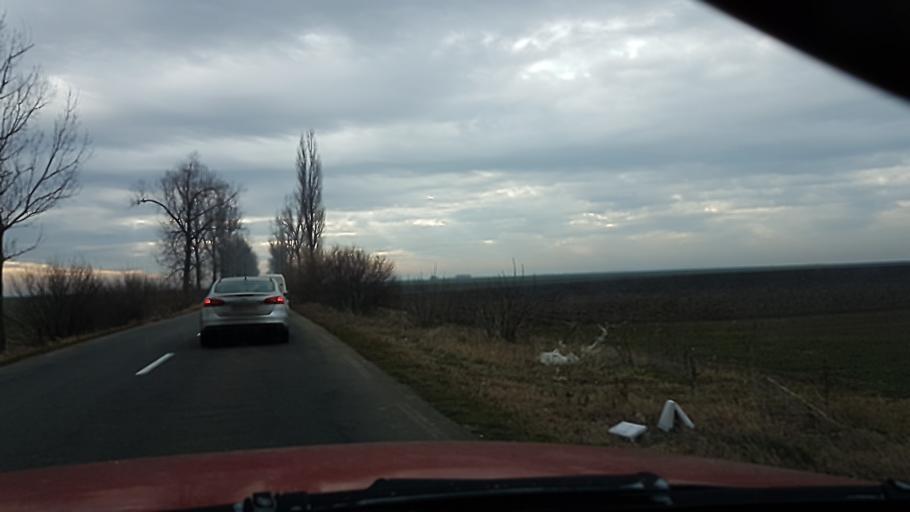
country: RO
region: Giurgiu
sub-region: Comuna Herasti
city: Herasti
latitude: 44.2389
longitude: 26.3601
